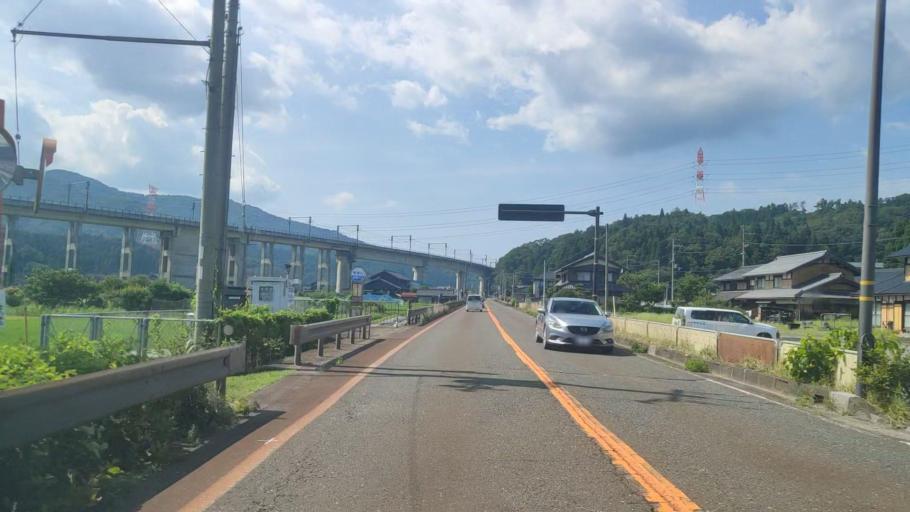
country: JP
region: Fukui
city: Tsuruga
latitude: 35.5285
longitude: 136.1570
